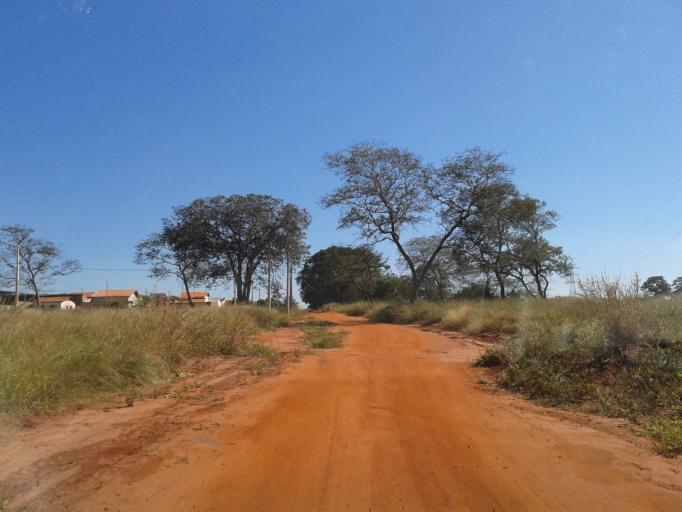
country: BR
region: Minas Gerais
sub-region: Santa Vitoria
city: Santa Vitoria
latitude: -18.8597
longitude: -50.1186
